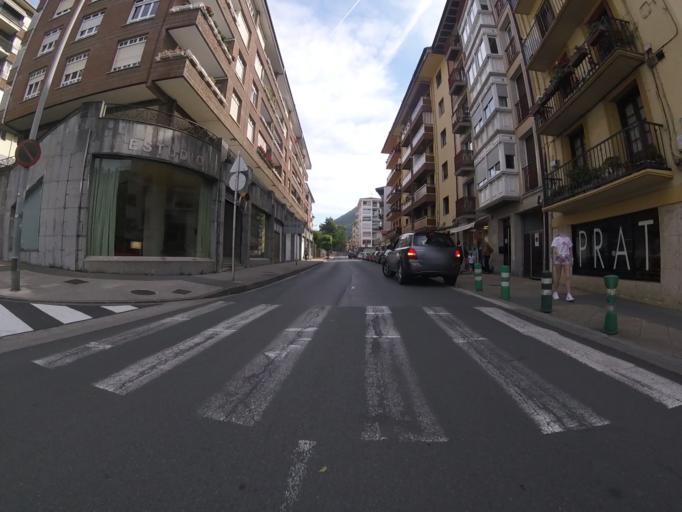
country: ES
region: Basque Country
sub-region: Provincia de Guipuzcoa
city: Azpeitia
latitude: 43.1815
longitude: -2.2695
